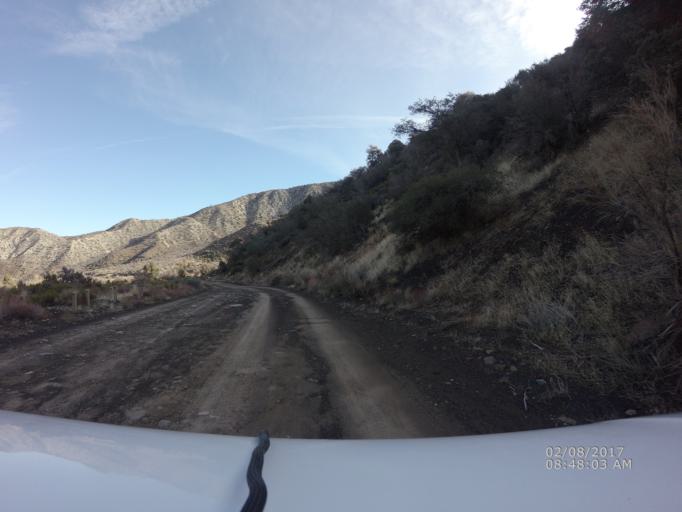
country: US
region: California
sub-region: San Bernardino County
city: Pinon Hills
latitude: 34.4049
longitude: -117.8238
